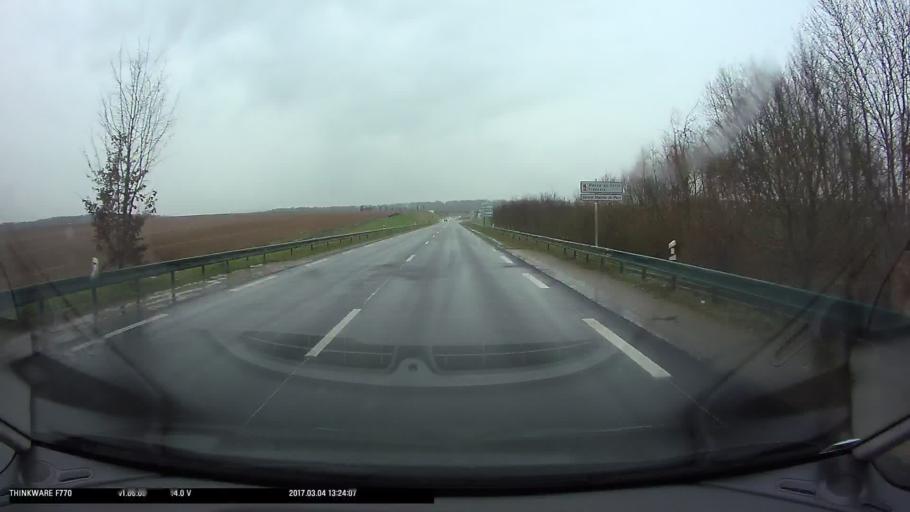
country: FR
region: Ile-de-France
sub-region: Departement du Val-d'Oise
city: Marines
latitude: 49.1375
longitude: 1.9706
